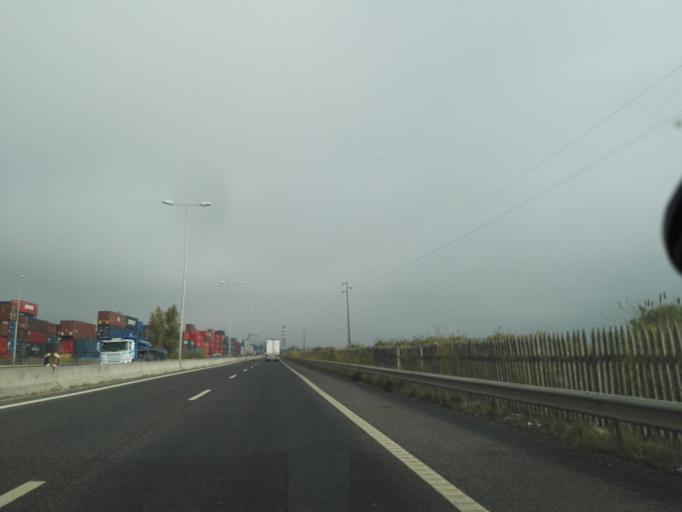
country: PT
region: Lisbon
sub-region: Loures
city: Sao Joao da Talha
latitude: 38.8159
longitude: -9.0875
